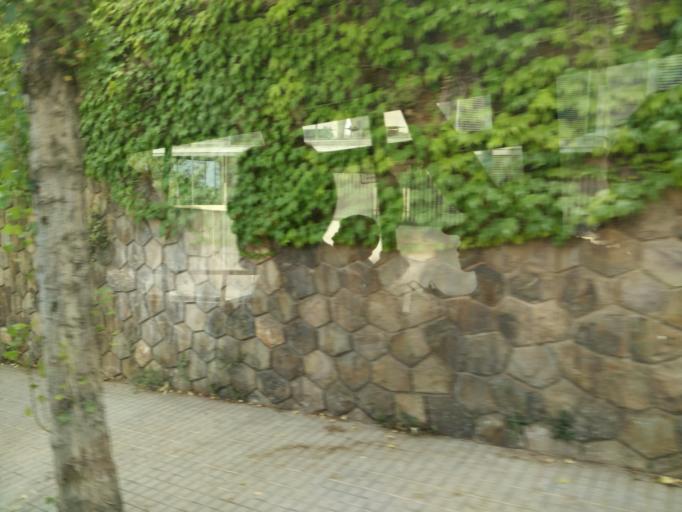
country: ES
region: Catalonia
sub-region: Provincia de Barcelona
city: Sarria-Sant Gervasi
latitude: 41.4142
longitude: 2.1302
